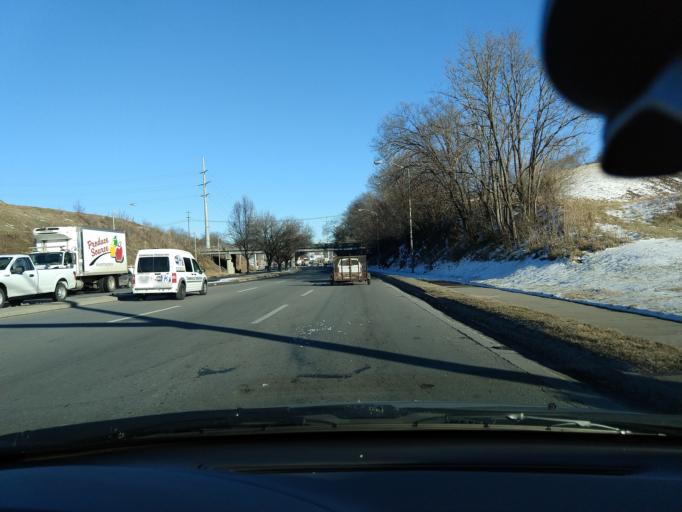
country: US
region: Virginia
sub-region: City of Roanoke
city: Roanoke
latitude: 37.2823
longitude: -79.9292
